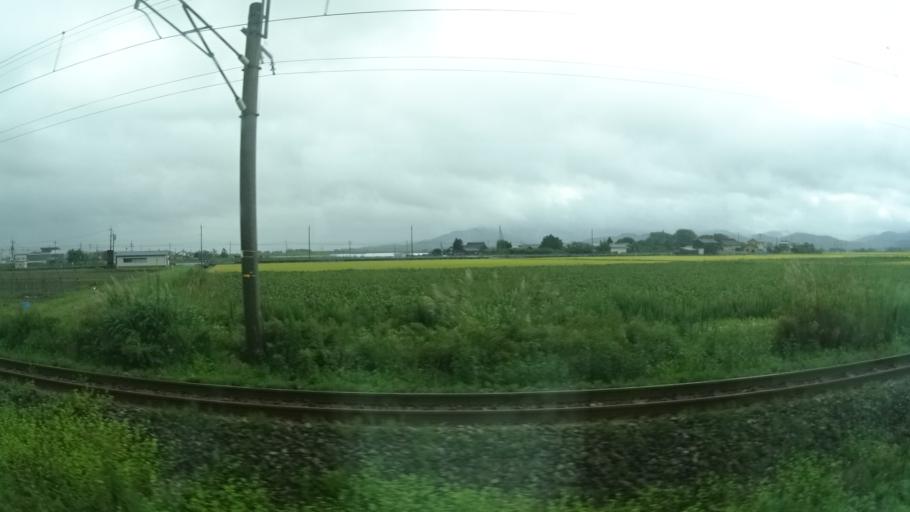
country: JP
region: Yamagata
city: Tsuruoka
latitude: 38.7409
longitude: 139.7582
